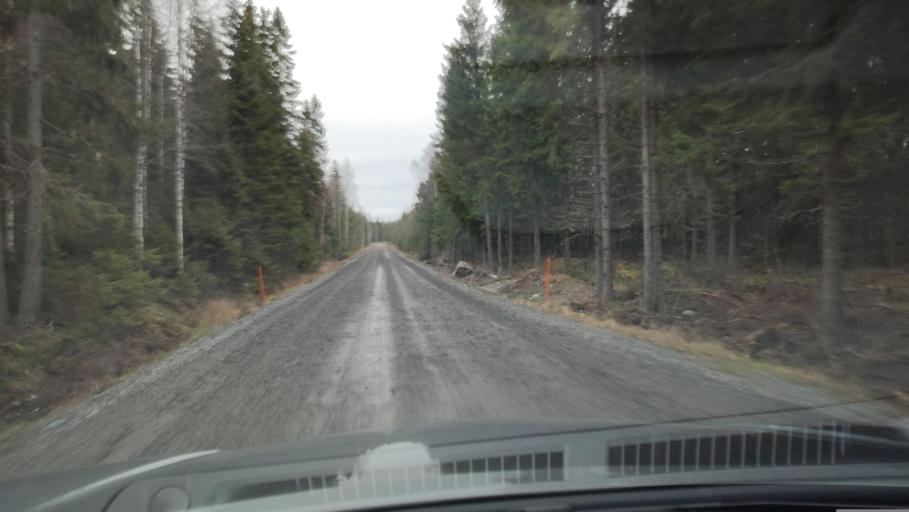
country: FI
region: Southern Ostrobothnia
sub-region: Suupohja
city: Karijoki
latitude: 62.1953
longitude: 21.5752
